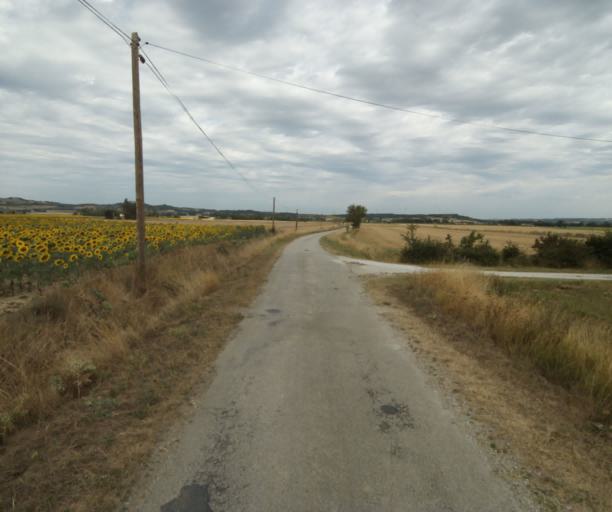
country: FR
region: Midi-Pyrenees
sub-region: Departement de la Haute-Garonne
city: Saint-Felix-Lauragais
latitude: 43.4364
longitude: 1.9364
